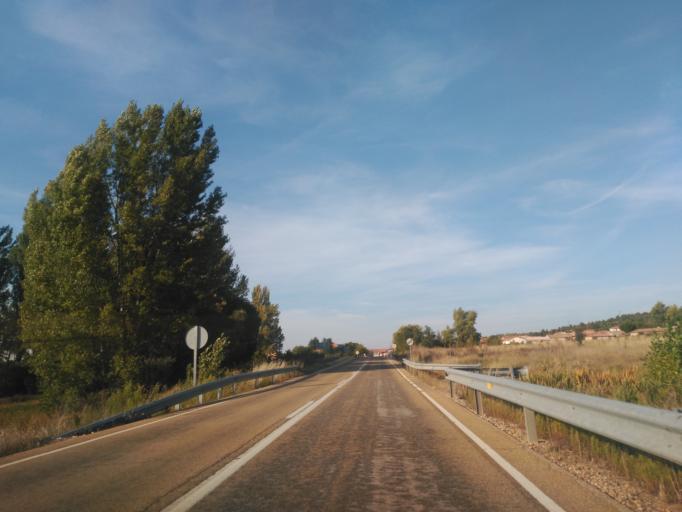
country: ES
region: Castille and Leon
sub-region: Provincia de Soria
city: Valdemaluque
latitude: 41.6700
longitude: -3.0477
